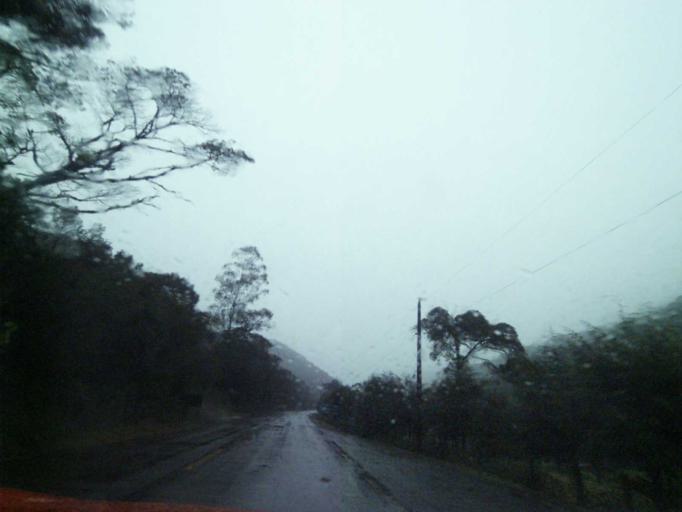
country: BR
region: Santa Catarina
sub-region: Anitapolis
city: Anitapolis
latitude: -27.7559
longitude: -49.0355
